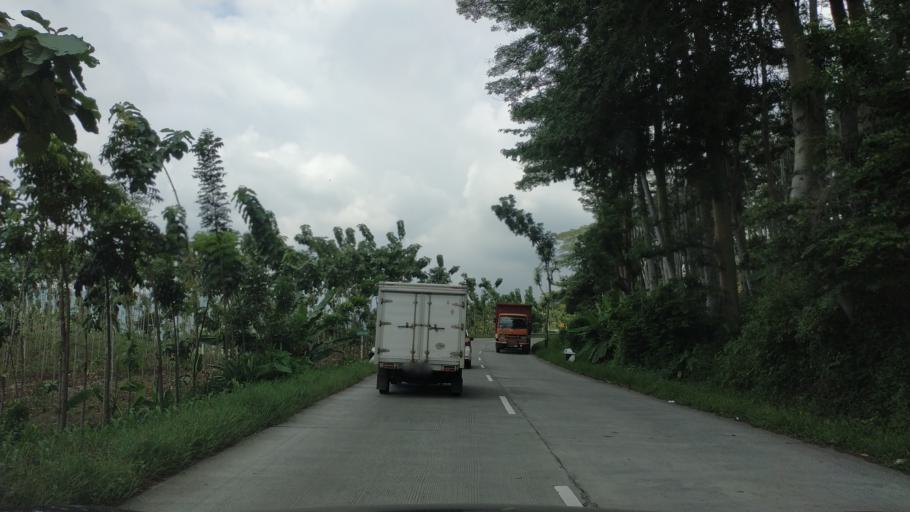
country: ID
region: Central Java
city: Weleri
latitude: -7.0058
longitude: 110.0606
